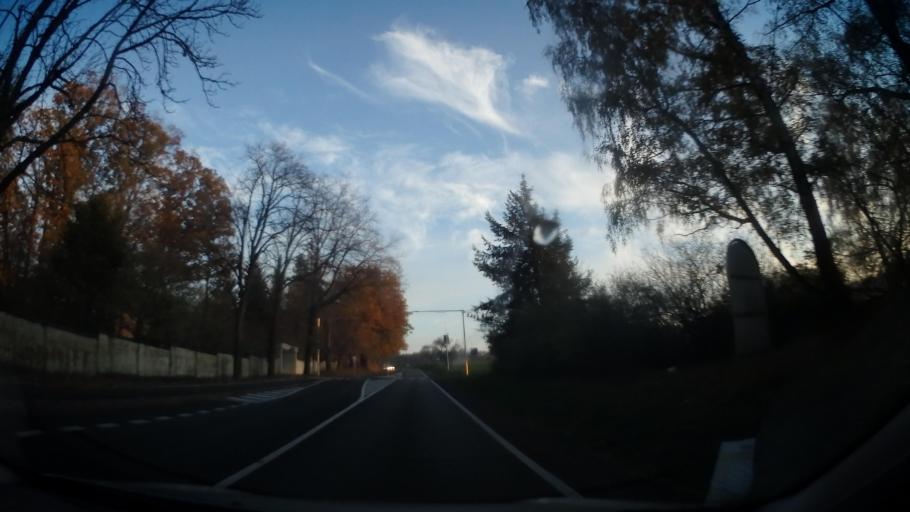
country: CZ
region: Central Bohemia
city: Vlasim
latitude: 49.6921
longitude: 14.9123
